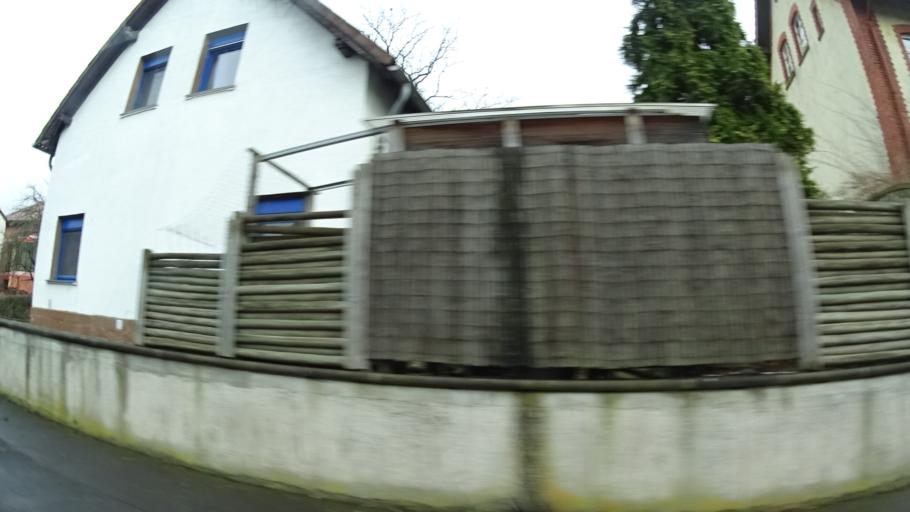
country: DE
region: Hesse
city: Tann
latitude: 50.6295
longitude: 10.0164
